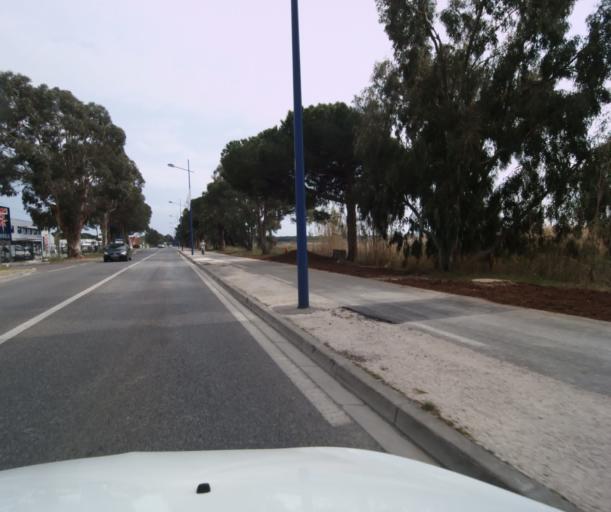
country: FR
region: Provence-Alpes-Cote d'Azur
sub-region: Departement du Var
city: Hyeres
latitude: 43.0861
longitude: 6.1470
